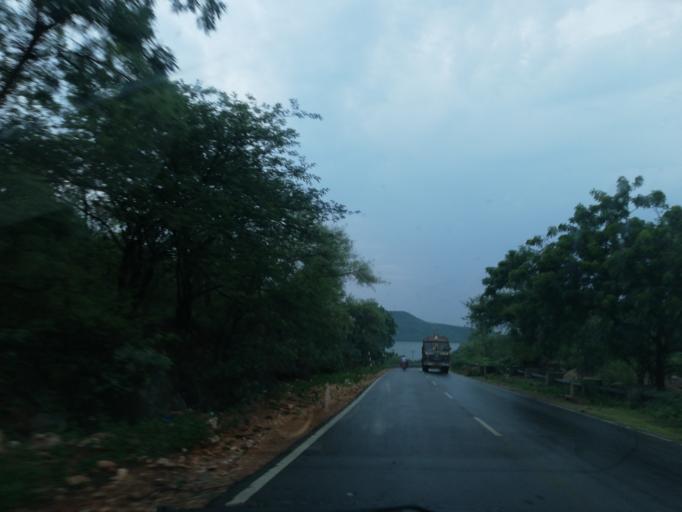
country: IN
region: Andhra Pradesh
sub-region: Guntur
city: Macherla
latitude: 16.6522
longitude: 79.2866
